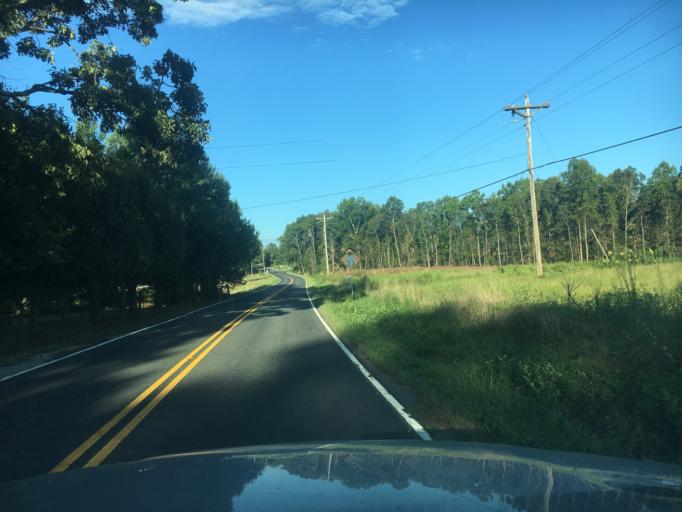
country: US
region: South Carolina
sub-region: Greenville County
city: Fountain Inn
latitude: 34.6113
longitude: -82.0951
